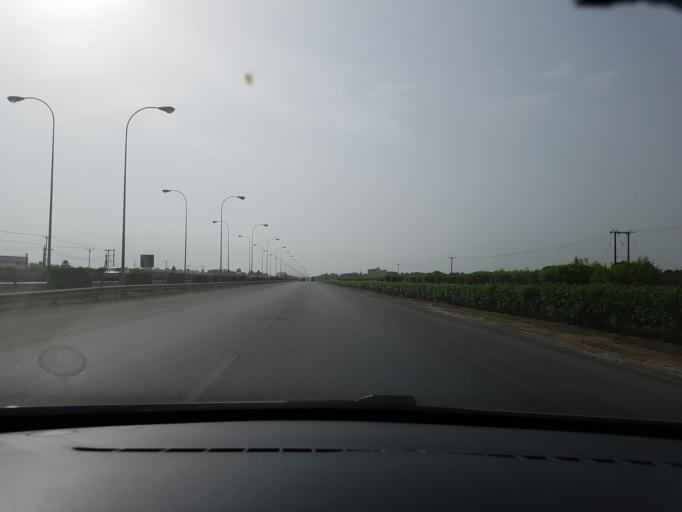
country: OM
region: Al Batinah
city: Al Sohar
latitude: 24.4054
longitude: 56.6542
